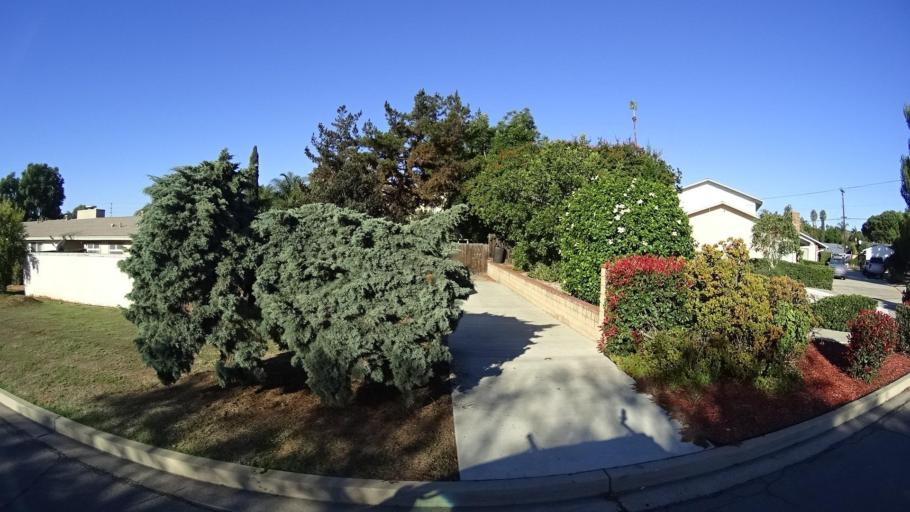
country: US
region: California
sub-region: San Diego County
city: Bonita
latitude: 32.6706
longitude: -117.0263
